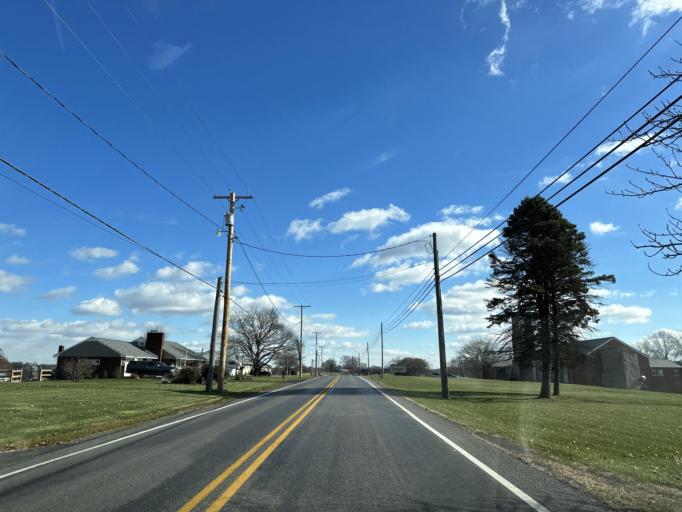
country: US
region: Pennsylvania
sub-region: Lebanon County
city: Myerstown
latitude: 40.4600
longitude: -76.2682
